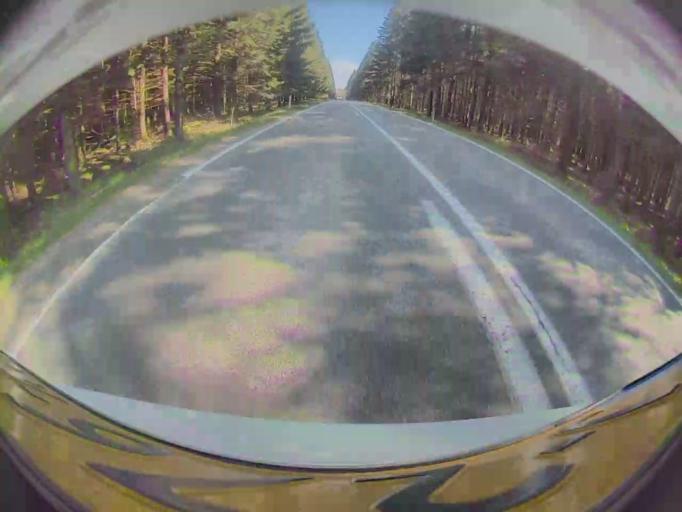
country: BE
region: Wallonia
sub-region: Province du Luxembourg
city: Libin
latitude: 50.0165
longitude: 5.2037
